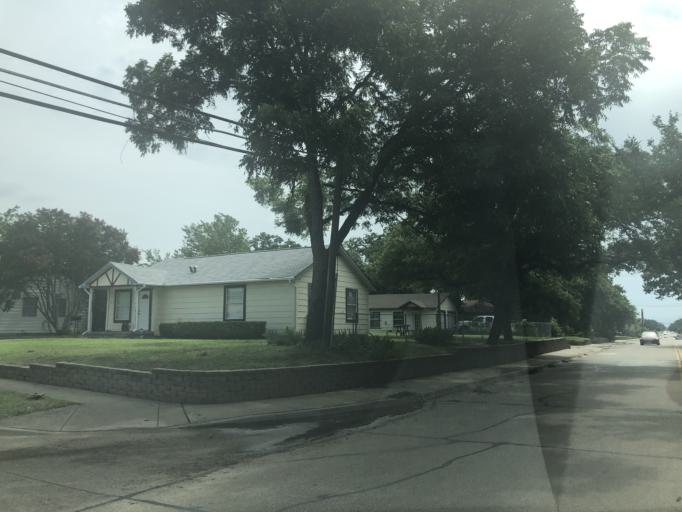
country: US
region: Texas
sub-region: Dallas County
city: Irving
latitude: 32.8086
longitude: -96.9558
